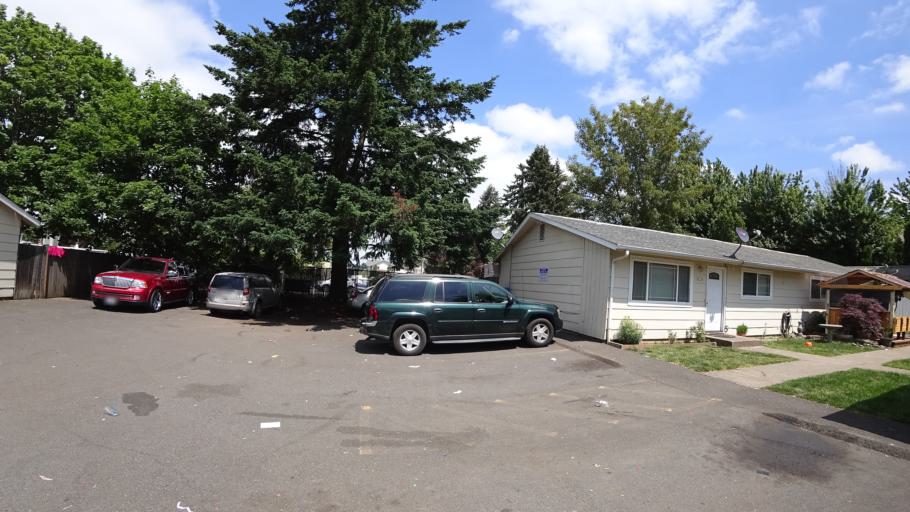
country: US
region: Oregon
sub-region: Multnomah County
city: Gresham
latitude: 45.5034
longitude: -122.4864
